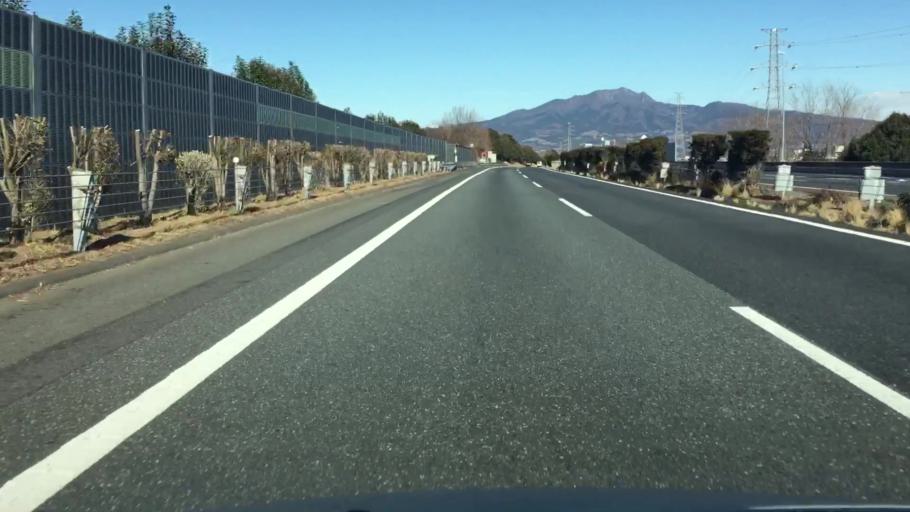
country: JP
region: Gunma
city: Shibukawa
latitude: 36.4595
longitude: 139.0123
